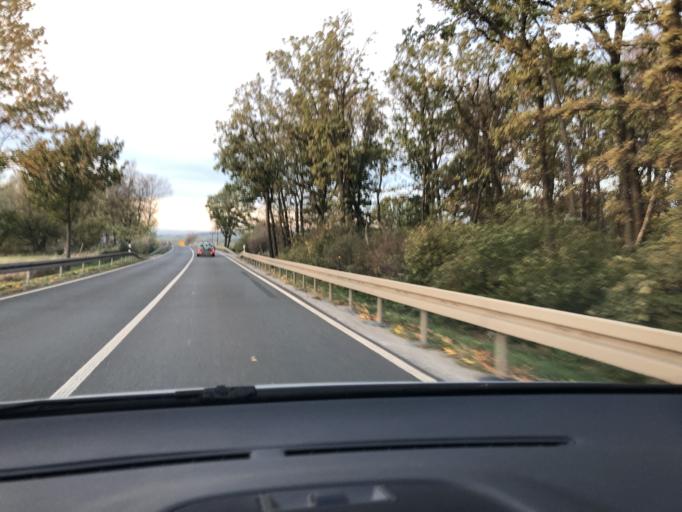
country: DE
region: Thuringia
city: Nohra
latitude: 50.9529
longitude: 11.2410
